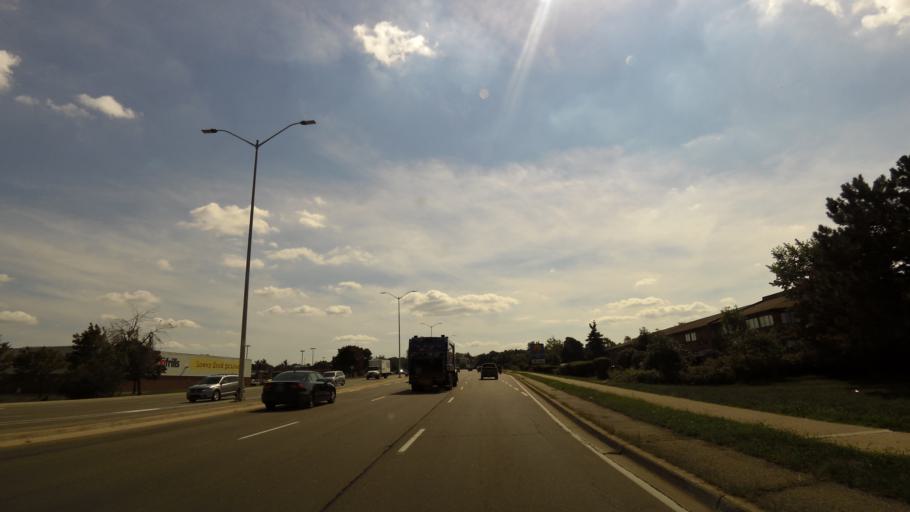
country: CA
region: Ontario
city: Mississauga
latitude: 43.5893
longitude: -79.7417
